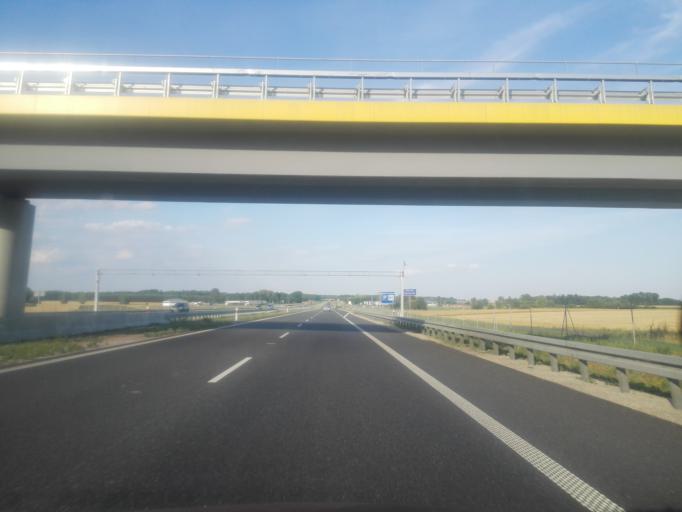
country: PL
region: Lodz Voivodeship
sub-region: Powiat wieruszowski
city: Galewice
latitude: 51.3093
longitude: 18.2339
